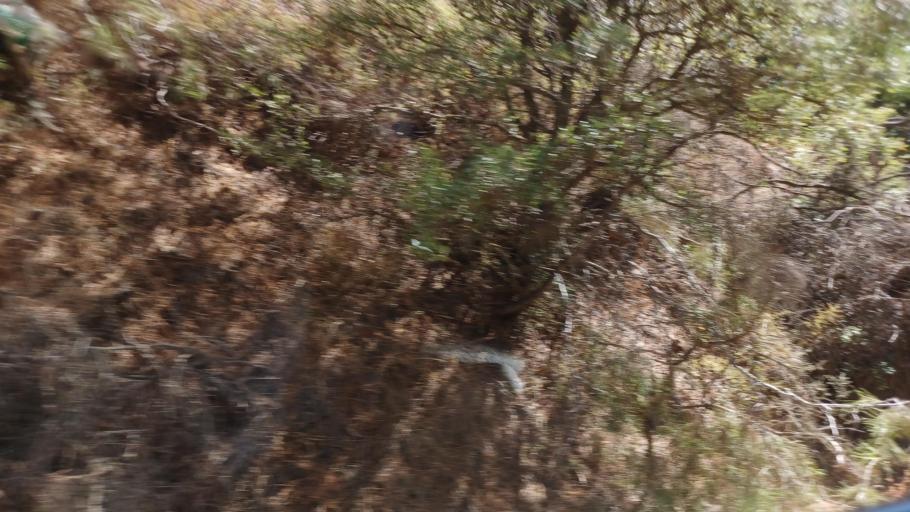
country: CY
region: Pafos
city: Mesogi
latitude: 34.9289
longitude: 32.6362
